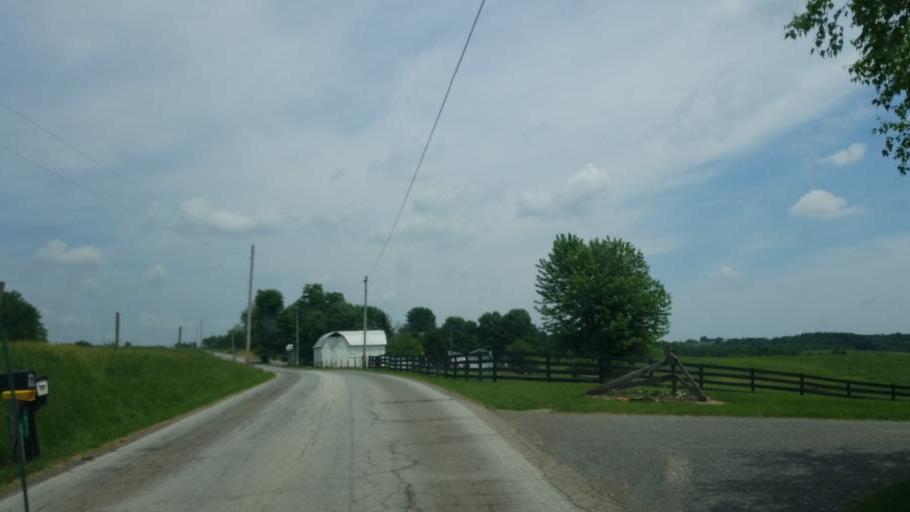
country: US
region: Ohio
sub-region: Holmes County
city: Millersburg
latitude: 40.4540
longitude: -81.7937
